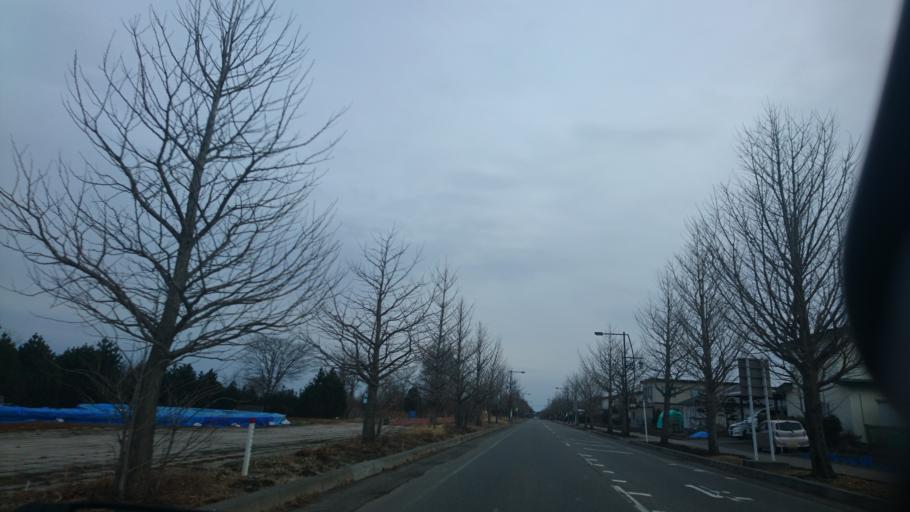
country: JP
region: Hokkaido
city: Otofuke
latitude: 42.9717
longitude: 143.1988
